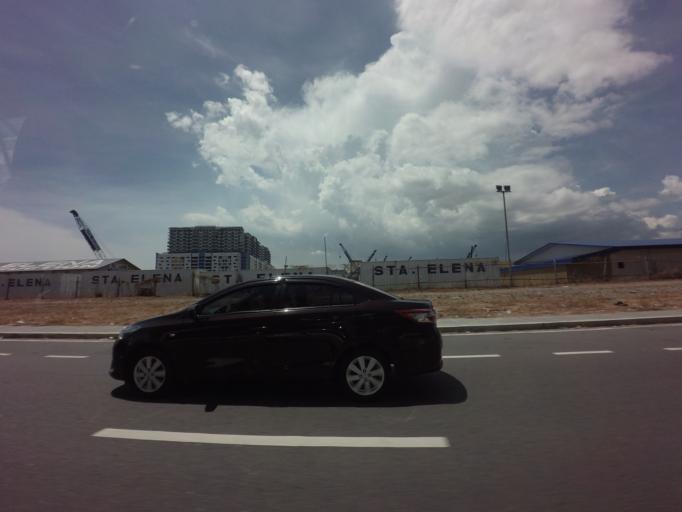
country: PH
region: Metro Manila
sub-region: Makati City
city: Makati City
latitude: 14.5175
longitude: 120.9894
